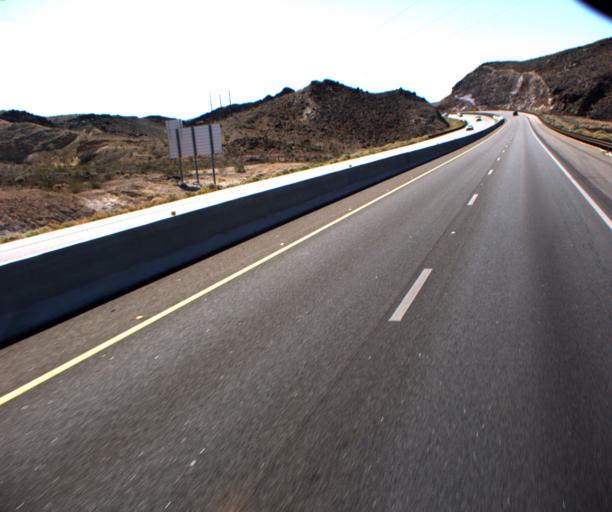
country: US
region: Nevada
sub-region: Clark County
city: Boulder City
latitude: 35.9899
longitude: -114.7160
